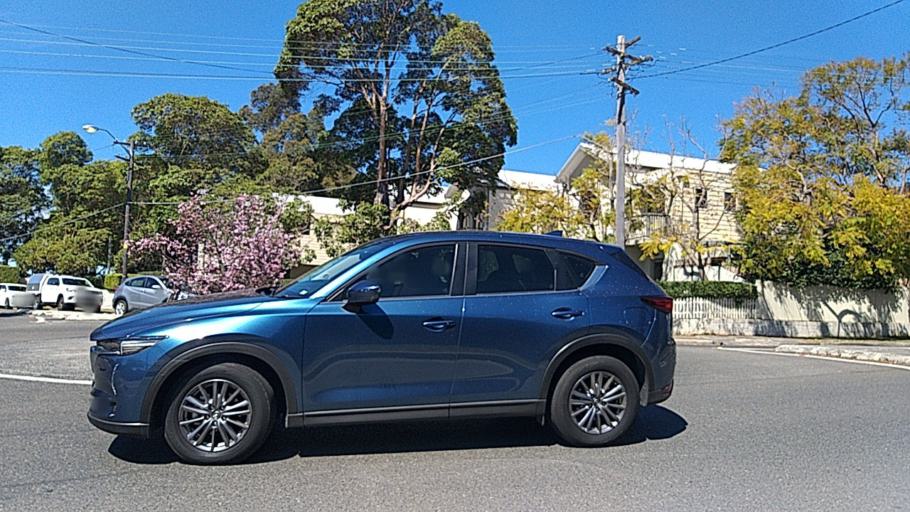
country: AU
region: New South Wales
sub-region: Ryde
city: East Ryde
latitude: -33.8224
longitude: 151.1252
